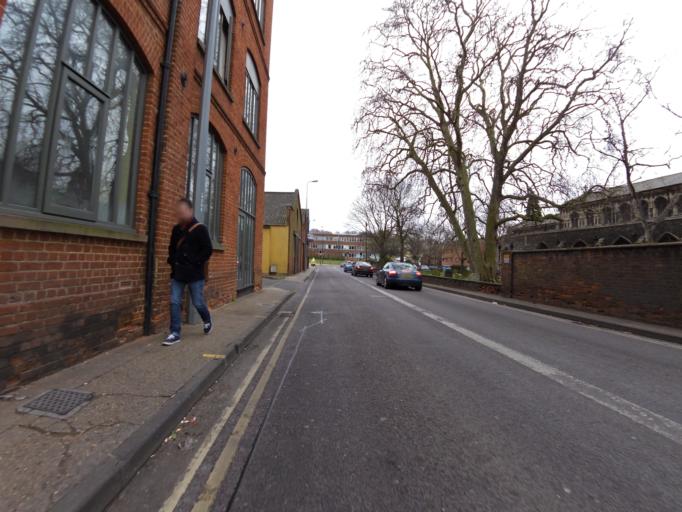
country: GB
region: England
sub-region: Suffolk
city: Ipswich
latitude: 52.0542
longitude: 1.1613
